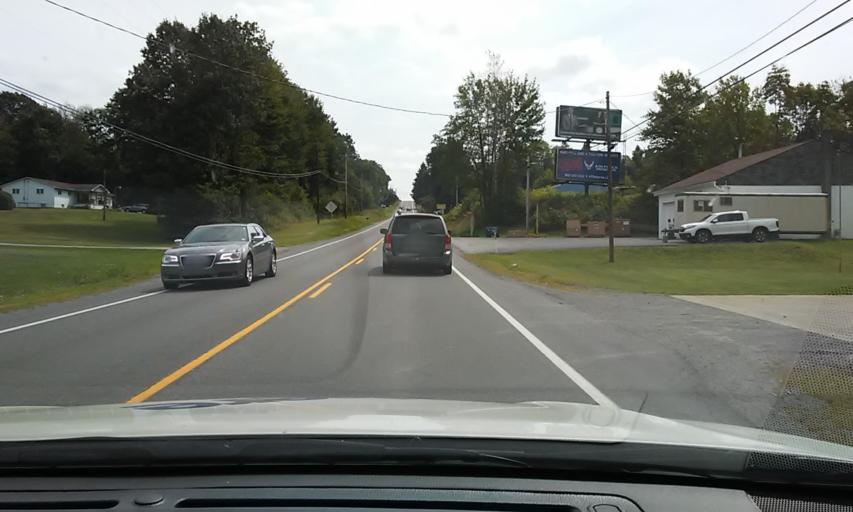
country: US
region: Pennsylvania
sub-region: Elk County
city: Saint Marys
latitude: 41.3577
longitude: -78.5492
